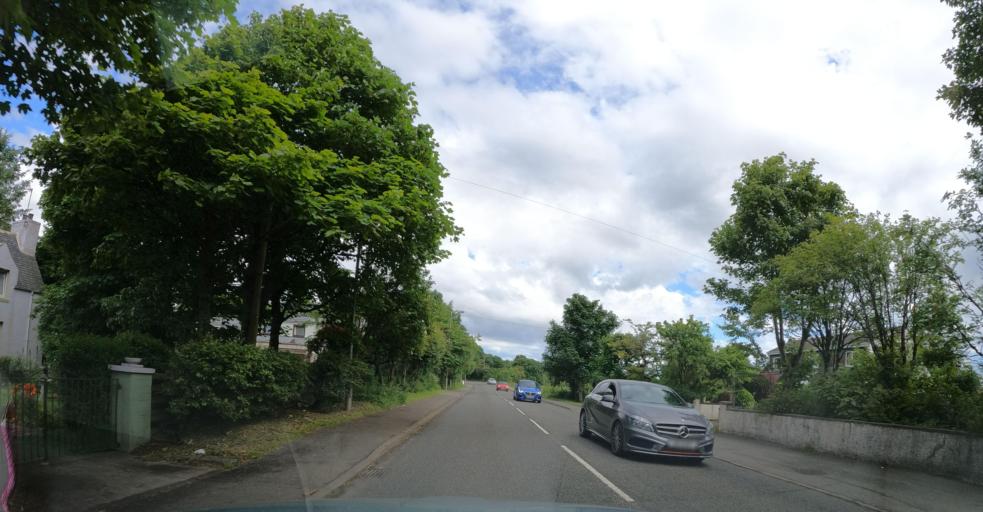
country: GB
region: Scotland
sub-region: Eilean Siar
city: Isle of Lewis
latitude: 58.2252
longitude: -6.3863
